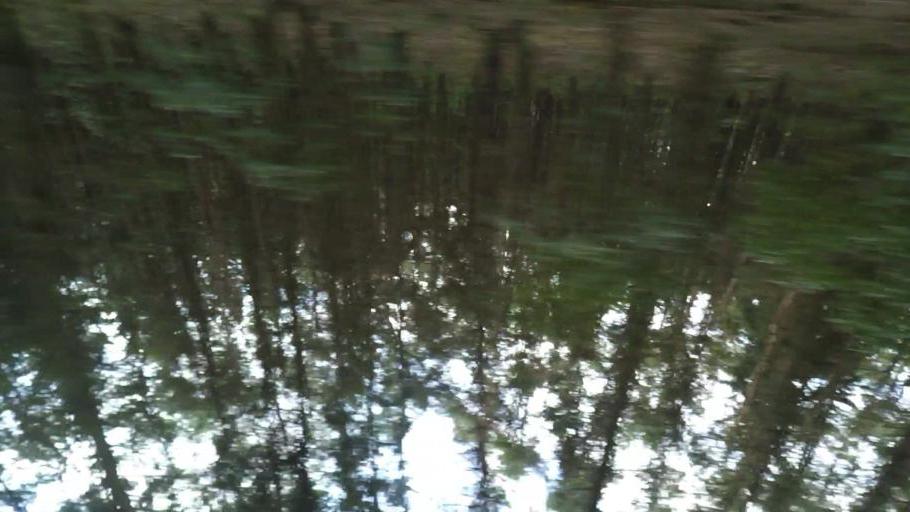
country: DK
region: Central Jutland
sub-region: Syddjurs Kommune
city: Ryomgard
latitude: 56.4787
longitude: 10.4878
